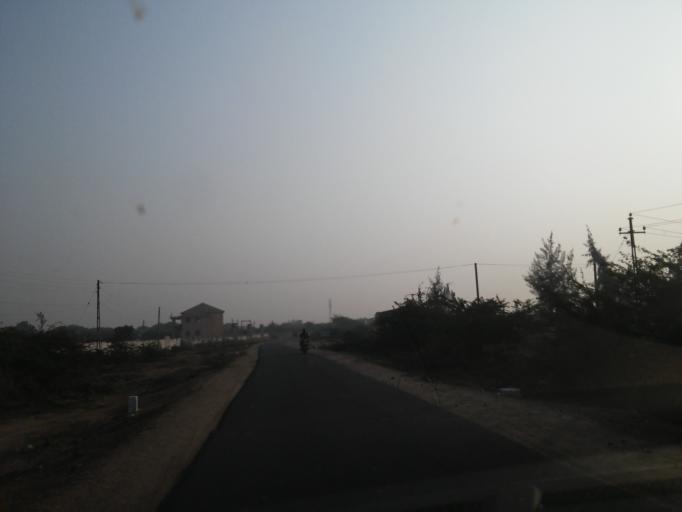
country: IN
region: Gujarat
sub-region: Kachchh
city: Mandvi
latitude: 22.8355
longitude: 69.3735
